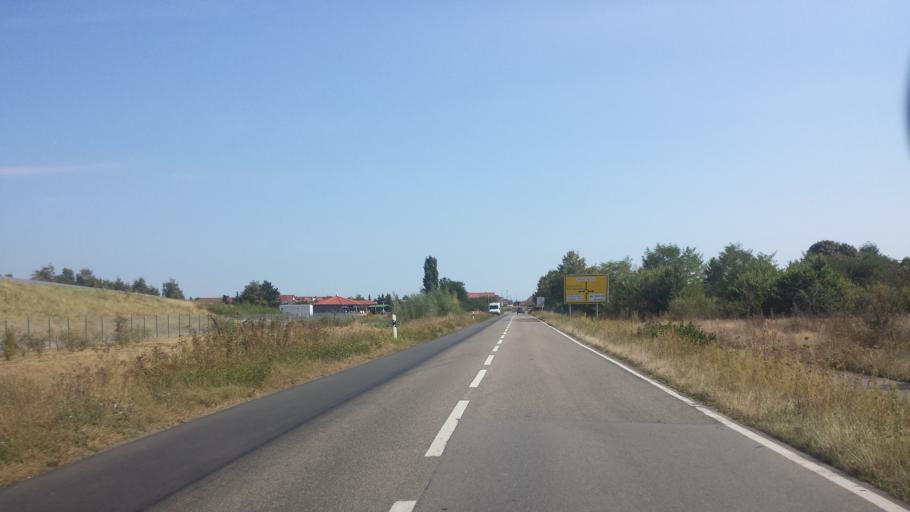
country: DE
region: Rheinland-Pfalz
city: Hassloch
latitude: 49.3633
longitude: 8.2334
